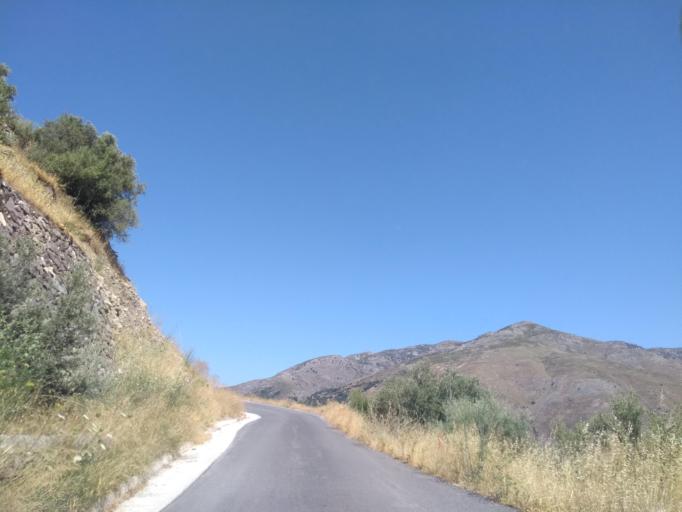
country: GR
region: Crete
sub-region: Nomos Chanias
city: Vryses
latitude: 35.3607
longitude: 23.5857
